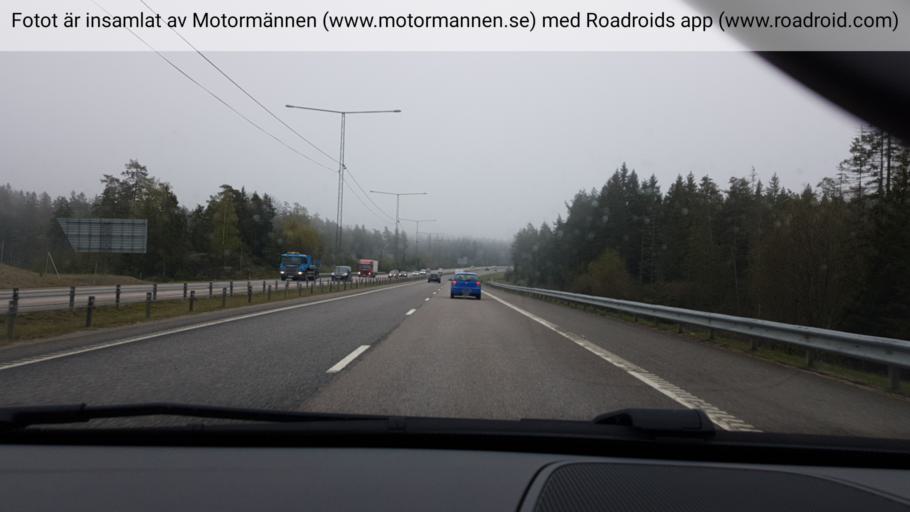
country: SE
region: Stockholm
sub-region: Haninge Kommun
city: Haninge
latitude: 59.1482
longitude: 18.1574
